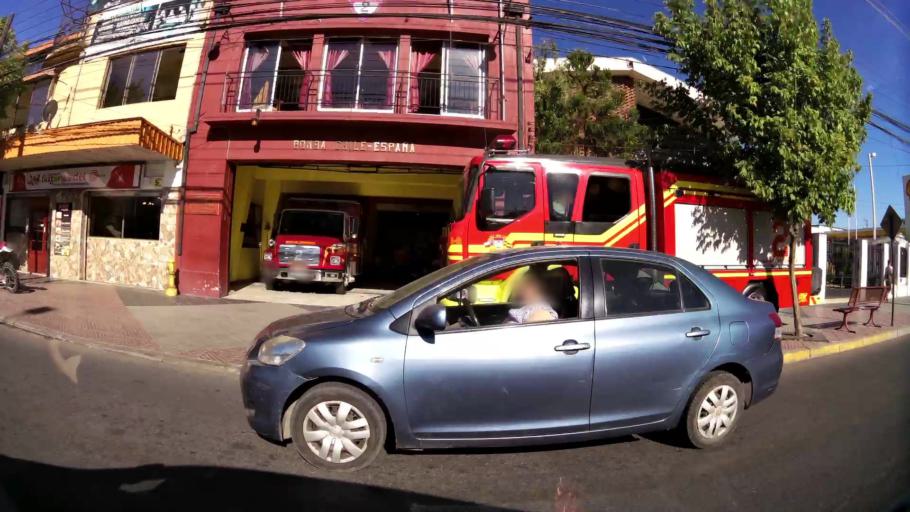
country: CL
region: O'Higgins
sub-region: Provincia de Colchagua
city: Chimbarongo
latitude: -34.5886
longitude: -70.9854
